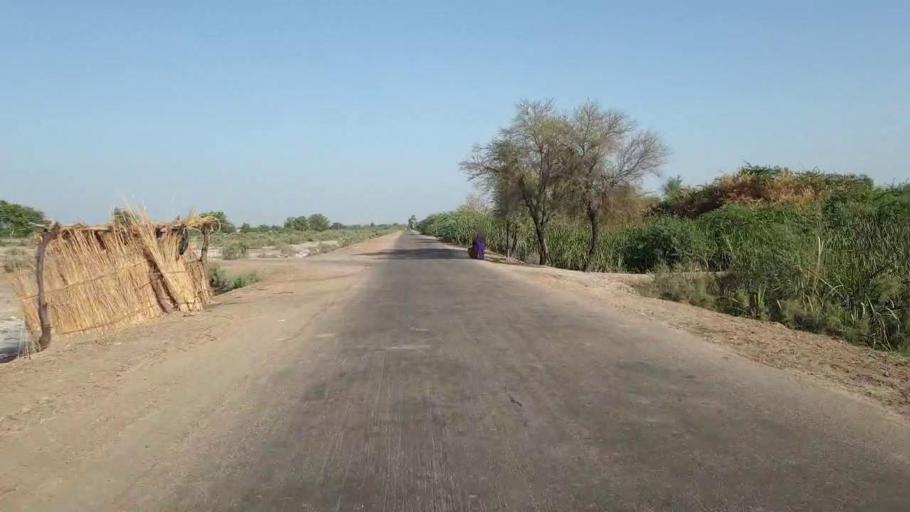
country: PK
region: Sindh
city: Nawabshah
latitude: 26.3878
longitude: 68.4523
